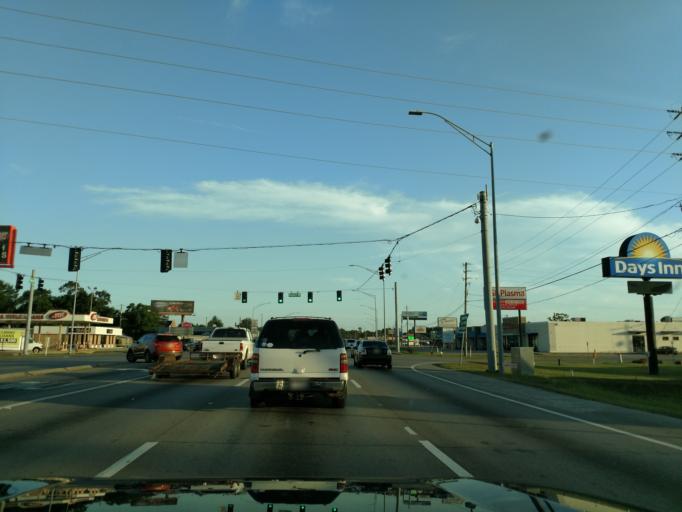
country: US
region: Mississippi
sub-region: Harrison County
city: West Gulfport
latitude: 30.4205
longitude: -89.0925
